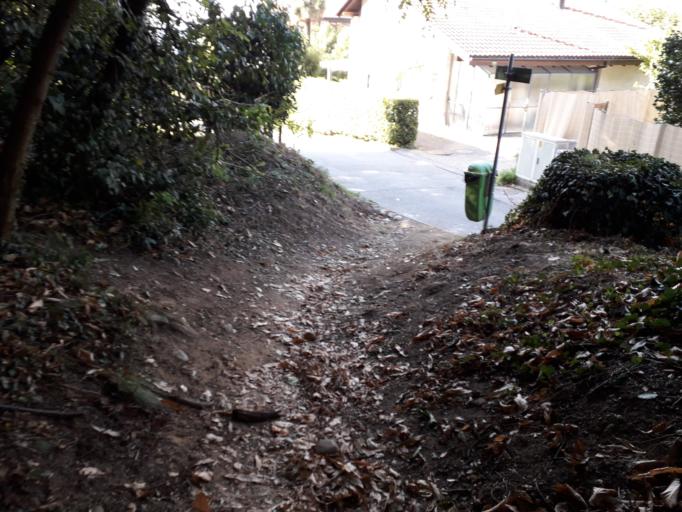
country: CH
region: Ticino
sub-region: Lugano District
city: Comano
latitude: 46.0396
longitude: 8.9541
